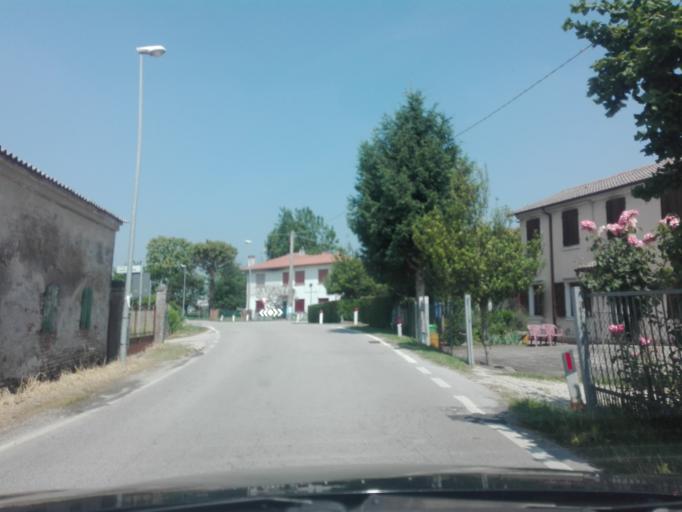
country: IT
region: Veneto
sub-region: Provincia di Rovigo
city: Pettorazza Grimani
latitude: 45.0638
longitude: 11.9836
